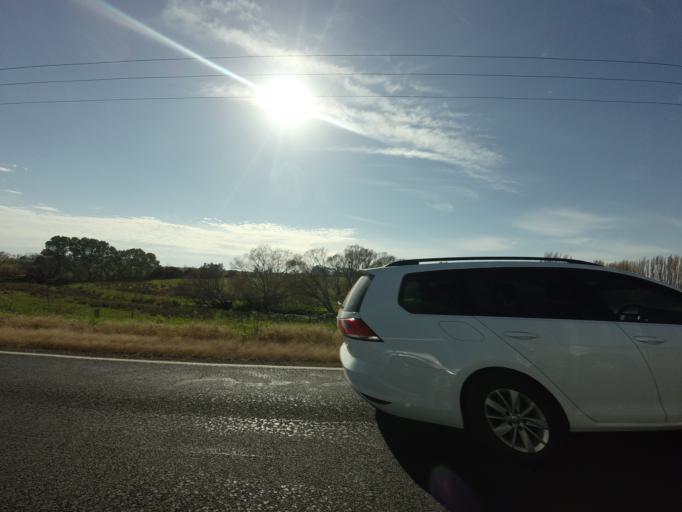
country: AU
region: Tasmania
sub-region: Meander Valley
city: Westbury
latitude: -41.5298
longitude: 146.9186
